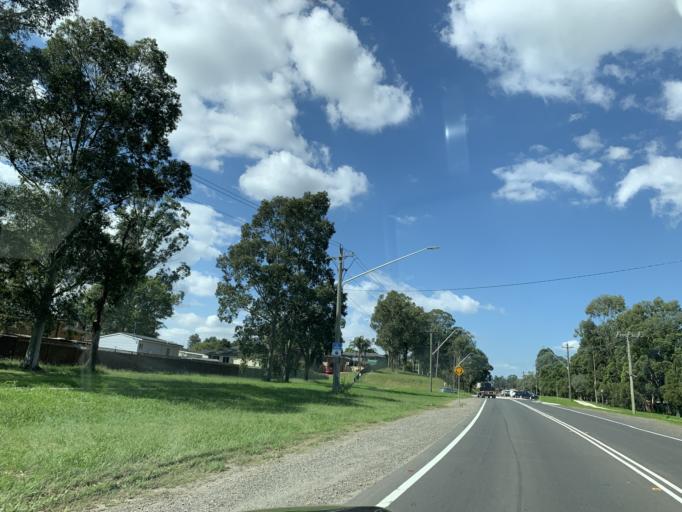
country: AU
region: New South Wales
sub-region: Penrith Municipality
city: Cambridge Park
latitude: -33.7341
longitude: 150.7107
